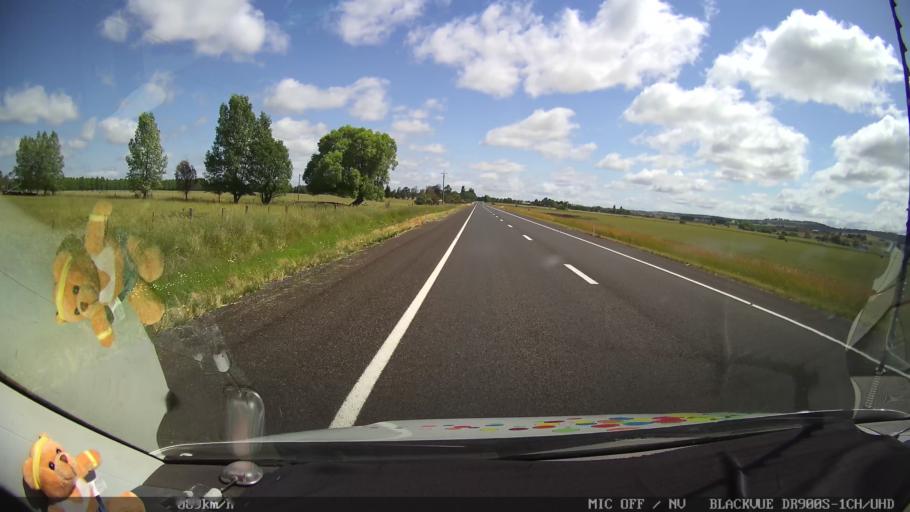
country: AU
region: New South Wales
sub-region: Glen Innes Severn
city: Glen Innes
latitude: -29.8299
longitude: 151.7379
